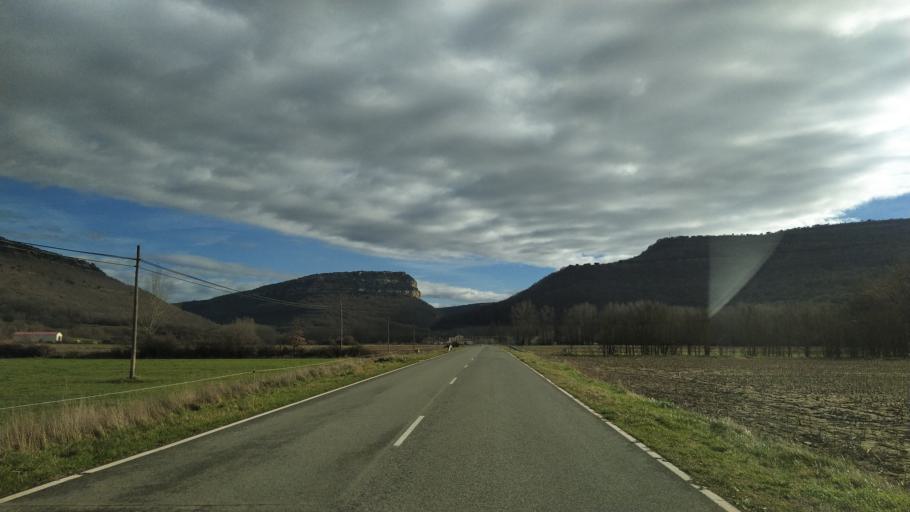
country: ES
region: Cantabria
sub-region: Provincia de Cantabria
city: San Martin de Elines
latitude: 42.8349
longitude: -3.8688
